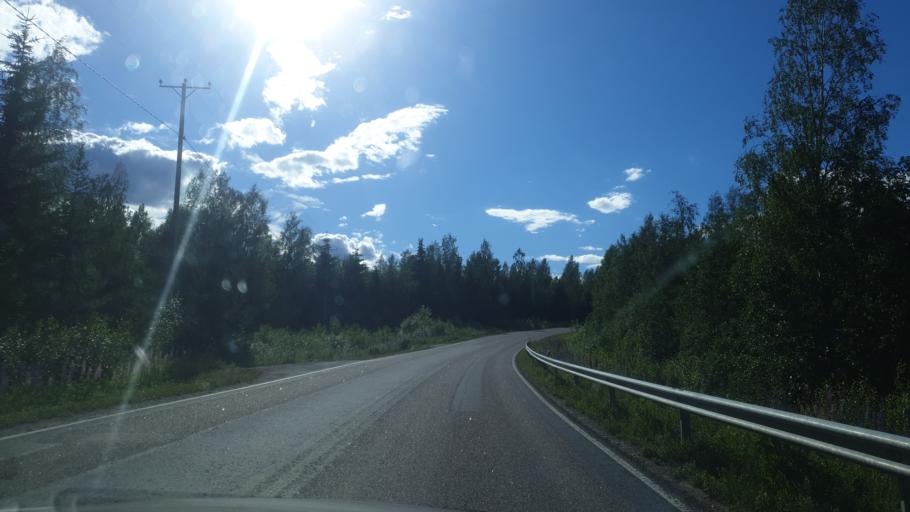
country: FI
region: Southern Savonia
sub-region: Mikkeli
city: Pertunmaa
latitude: 61.5255
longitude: 26.6254
